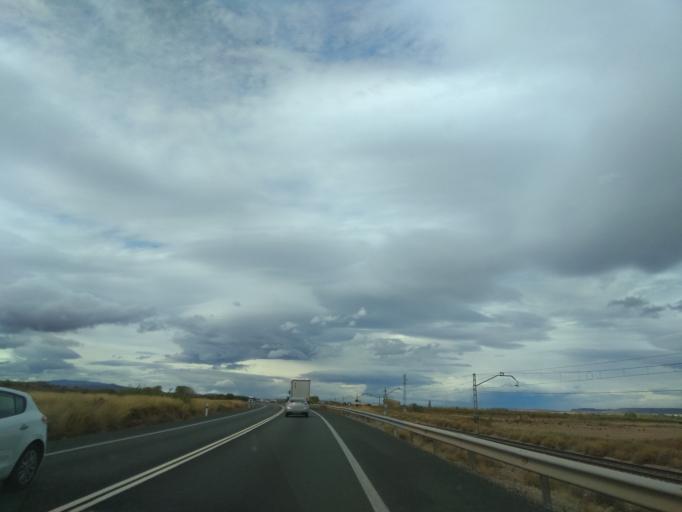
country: ES
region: La Rioja
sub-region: Provincia de La Rioja
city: Rincon de Soto
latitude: 42.2127
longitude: -1.8109
